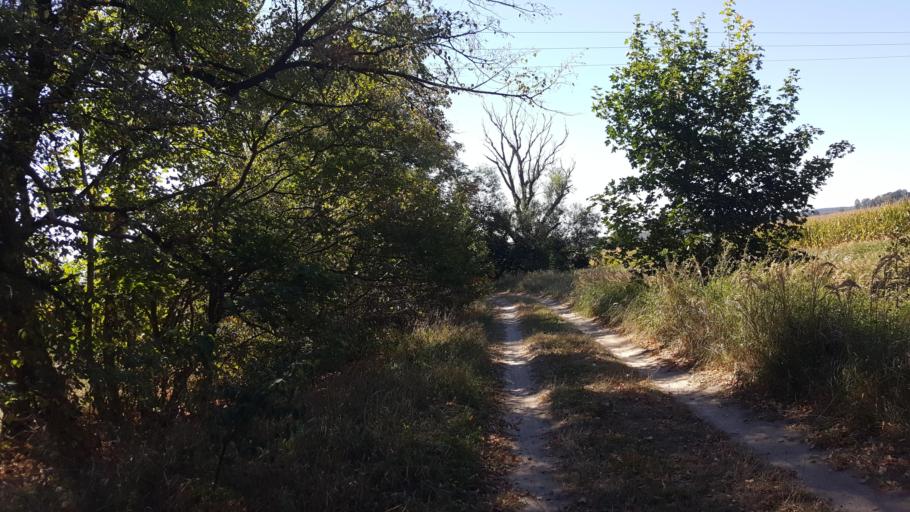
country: PL
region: Lublin Voivodeship
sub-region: Powiat bialski
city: Terespol
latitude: 52.2163
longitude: 23.5089
